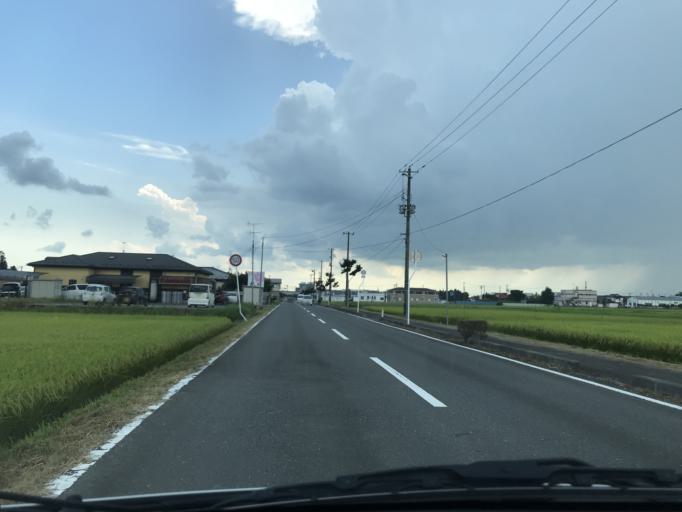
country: JP
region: Iwate
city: Ichinoseki
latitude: 38.7588
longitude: 141.0709
